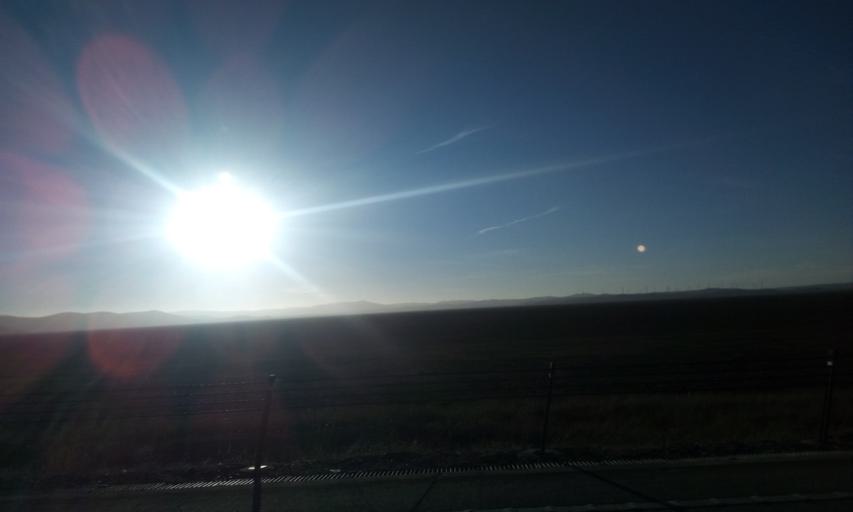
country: AU
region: New South Wales
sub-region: Yass Valley
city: Gundaroo
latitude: -35.0708
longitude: 149.3739
